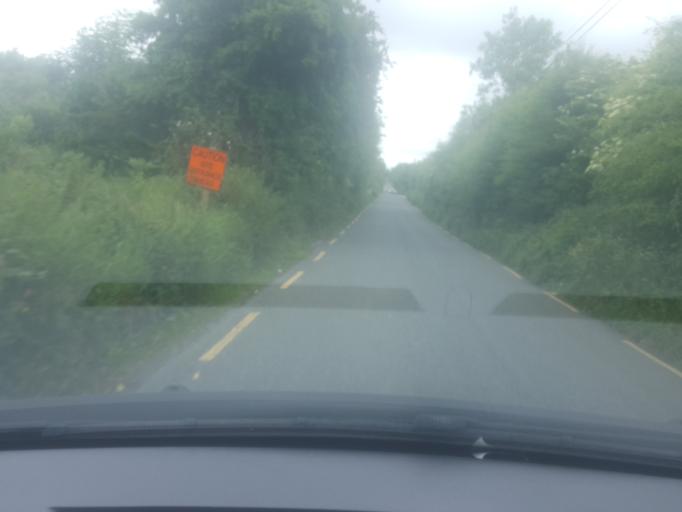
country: IE
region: Munster
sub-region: Ciarrai
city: Cill Airne
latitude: 52.0827
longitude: -9.5069
